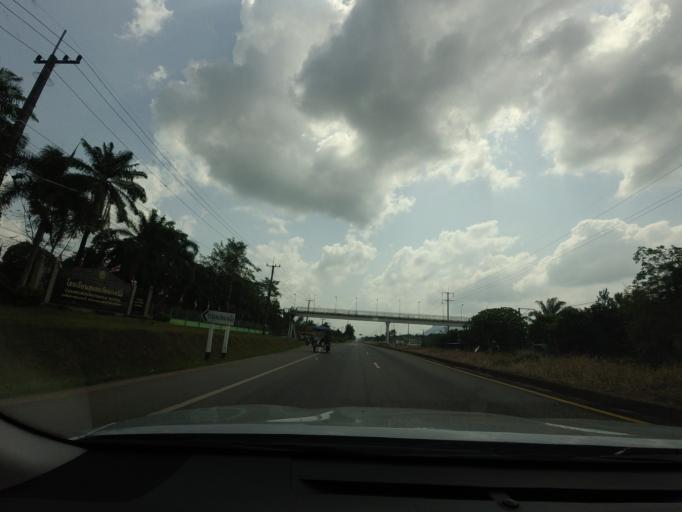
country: TH
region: Phangnga
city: Thap Put
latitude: 8.5047
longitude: 98.6939
